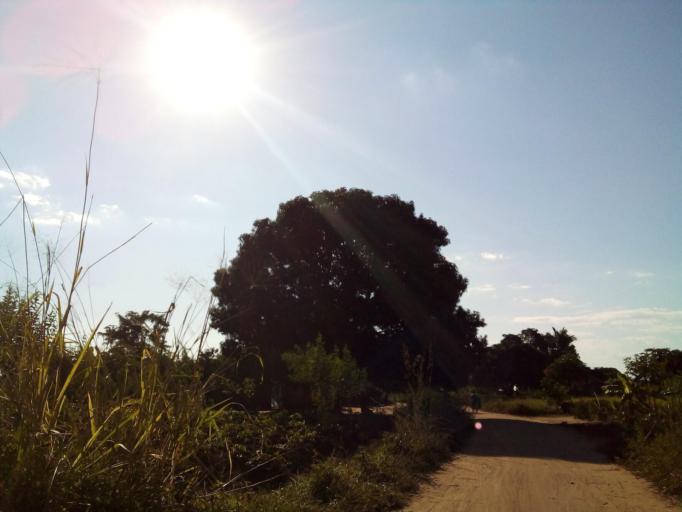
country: MZ
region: Zambezia
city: Quelimane
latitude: -17.5308
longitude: 36.6833
